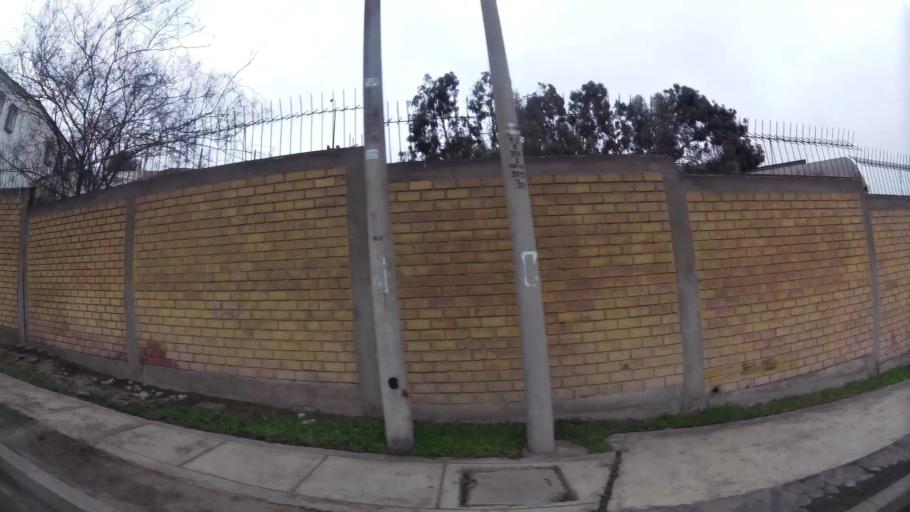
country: PE
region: Lima
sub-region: Lima
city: La Molina
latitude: -12.0793
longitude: -76.9238
